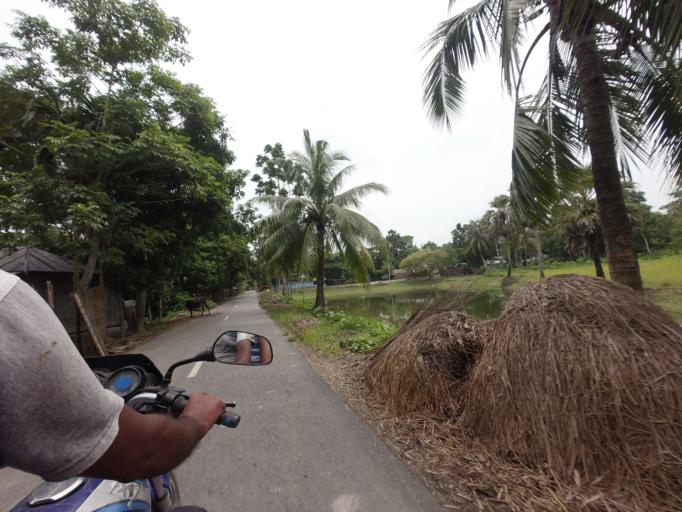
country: BD
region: Khulna
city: Kalia
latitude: 23.1003
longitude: 89.6490
